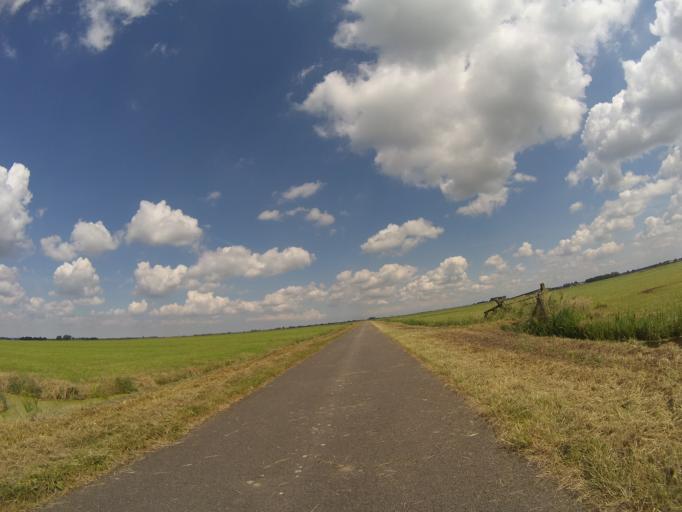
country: NL
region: Utrecht
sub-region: Gemeente Bunschoten
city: Spakenburg
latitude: 52.2275
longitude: 5.3324
